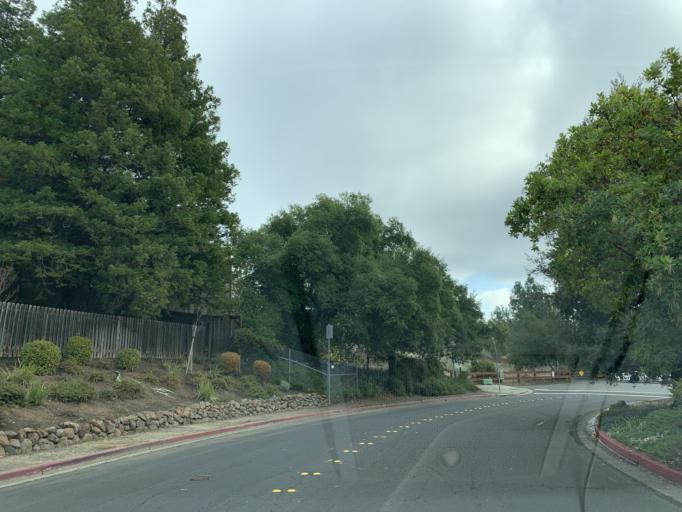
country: US
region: California
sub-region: Contra Costa County
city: Saranap
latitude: 37.8794
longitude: -122.0704
